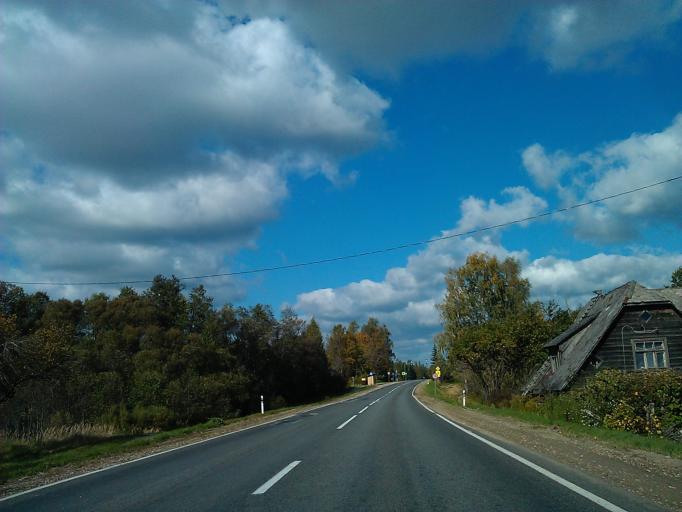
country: LV
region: Livani
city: Livani
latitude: 56.2520
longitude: 26.2078
